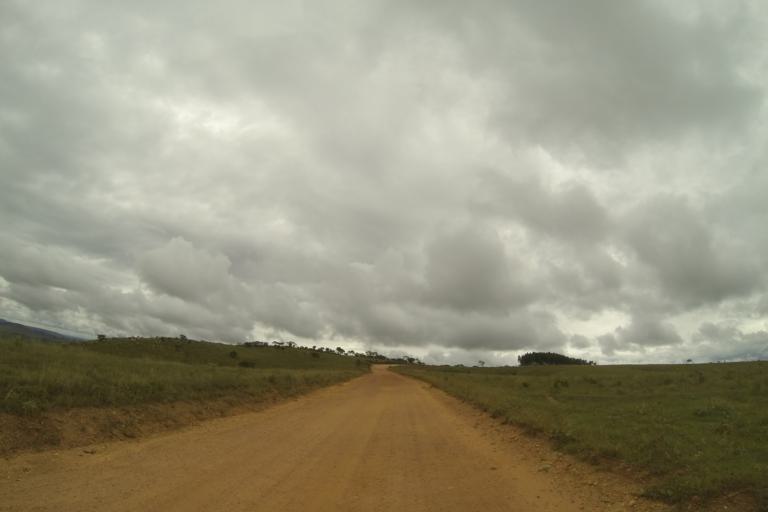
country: BR
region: Minas Gerais
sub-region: Ibia
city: Ibia
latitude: -19.7421
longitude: -46.4777
